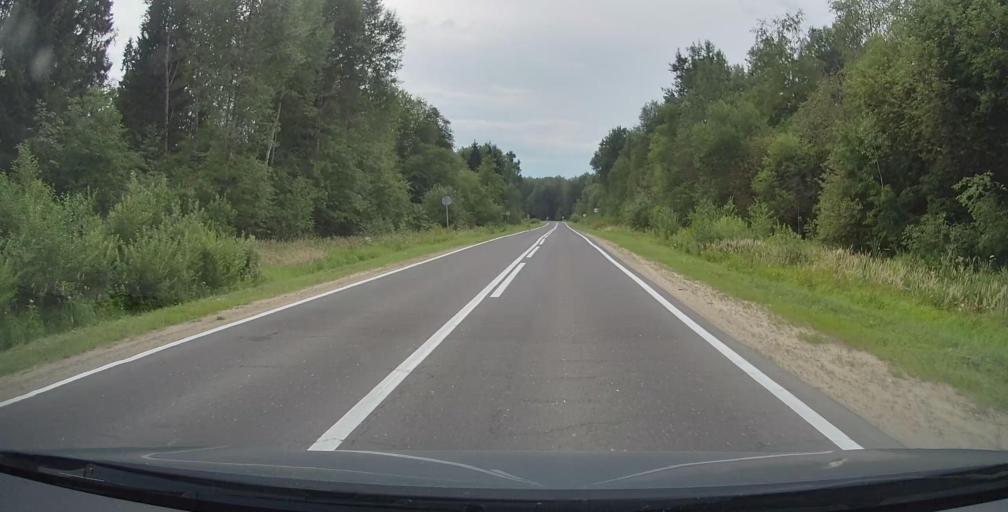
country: RU
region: Jaroslavl
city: Rybinsk
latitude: 57.9593
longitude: 38.7221
